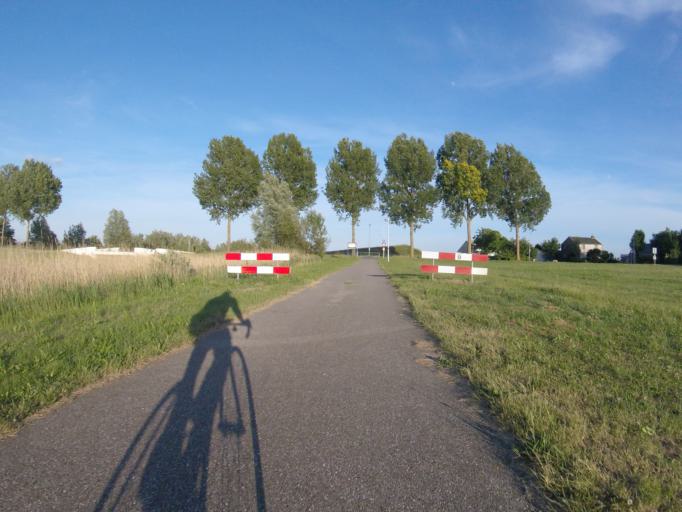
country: NL
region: North Holland
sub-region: Gemeente Haarlemmermeer
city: Hoofddorp
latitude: 52.3012
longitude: 4.7247
